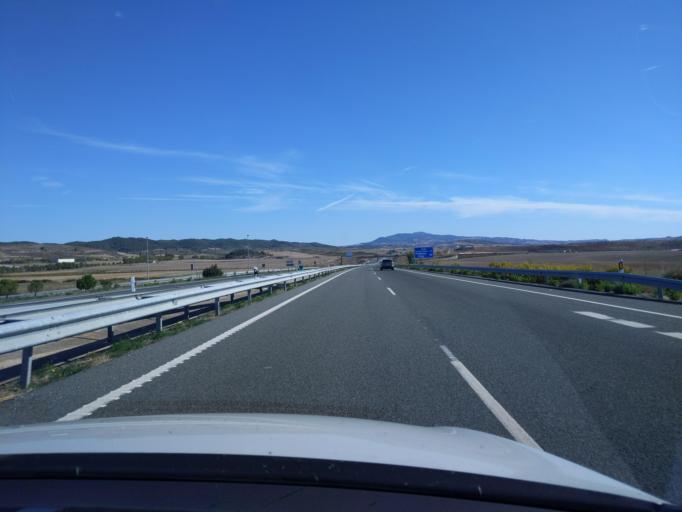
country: ES
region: Navarre
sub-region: Provincia de Navarra
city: Los Arcos
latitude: 42.5597
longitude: -2.1823
